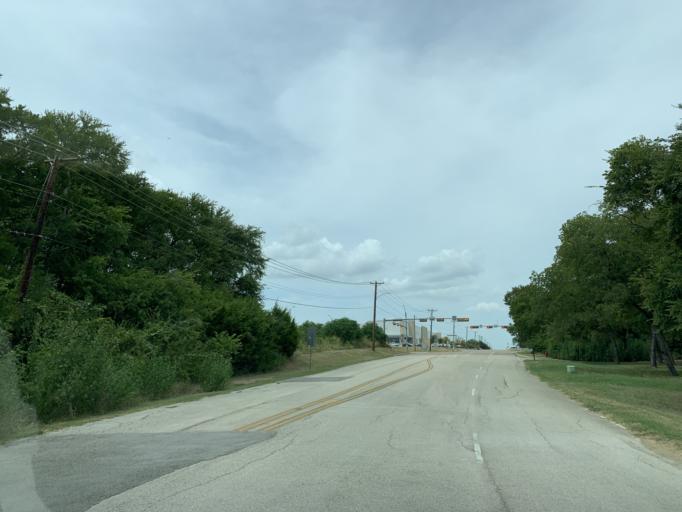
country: US
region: Texas
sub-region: Dallas County
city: Grand Prairie
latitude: 32.6682
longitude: -97.0309
